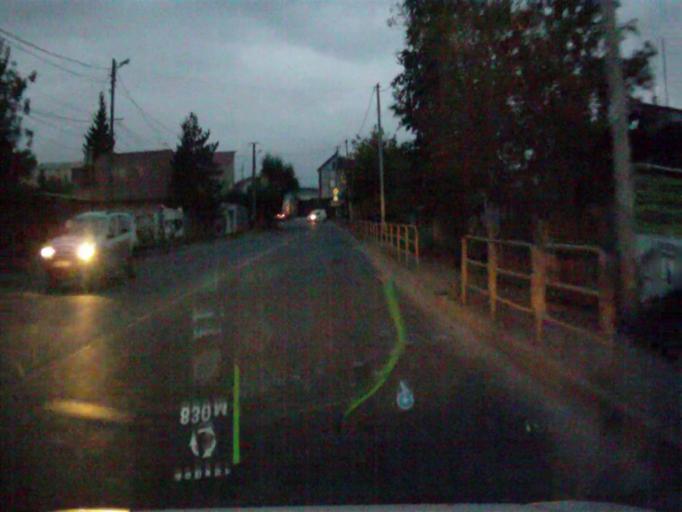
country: RU
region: Chelyabinsk
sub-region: Gorod Chelyabinsk
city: Chelyabinsk
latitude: 55.1554
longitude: 61.3021
